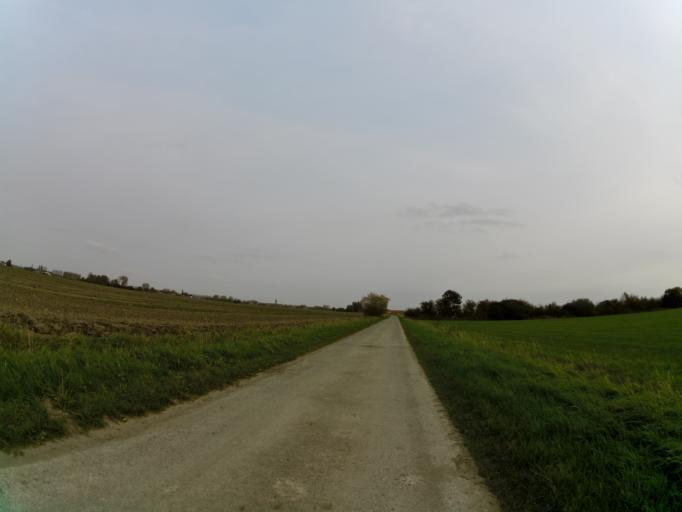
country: BE
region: Flanders
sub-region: Provincie West-Vlaanderen
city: Jabbeke
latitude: 51.2084
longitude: 3.0469
